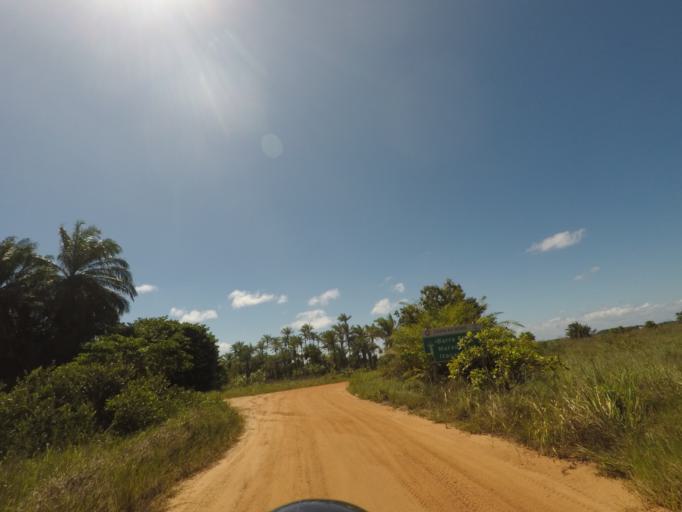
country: BR
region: Bahia
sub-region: Camamu
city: Camamu
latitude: -13.9500
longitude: -38.9381
